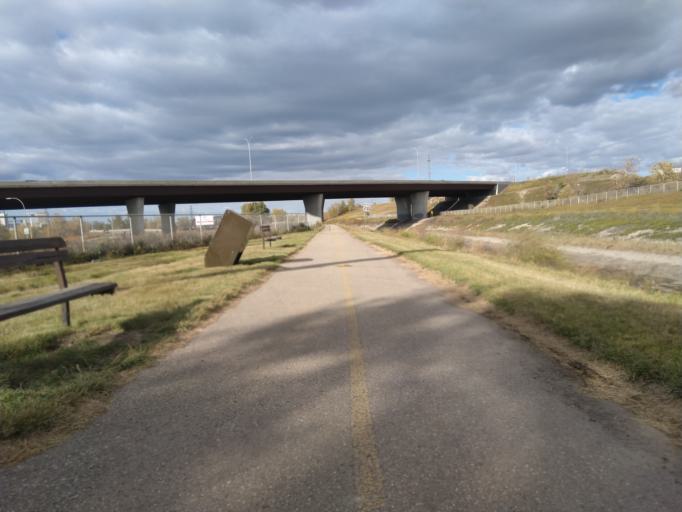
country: CA
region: Alberta
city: Calgary
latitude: 51.0094
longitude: -114.0097
